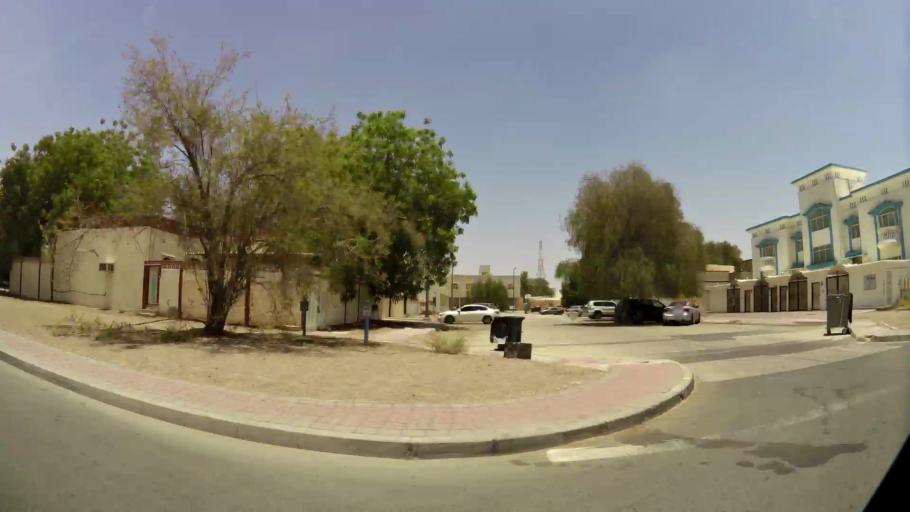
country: OM
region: Al Buraimi
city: Al Buraymi
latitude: 24.2611
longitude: 55.7341
